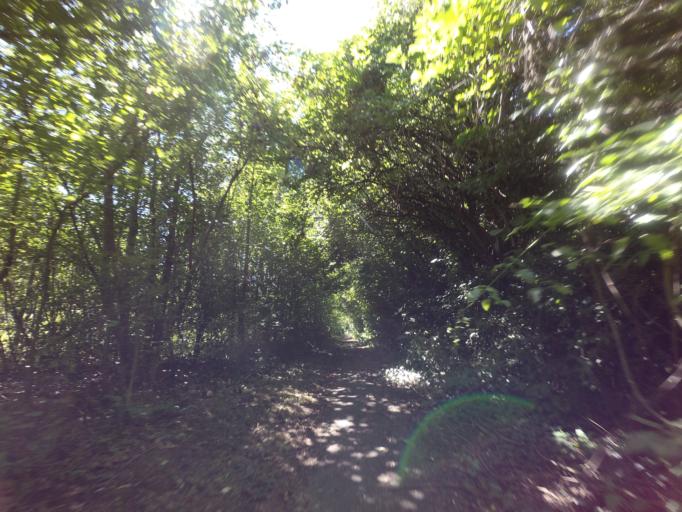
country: GB
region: England
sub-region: Kent
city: Eastry
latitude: 51.2266
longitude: 1.3018
